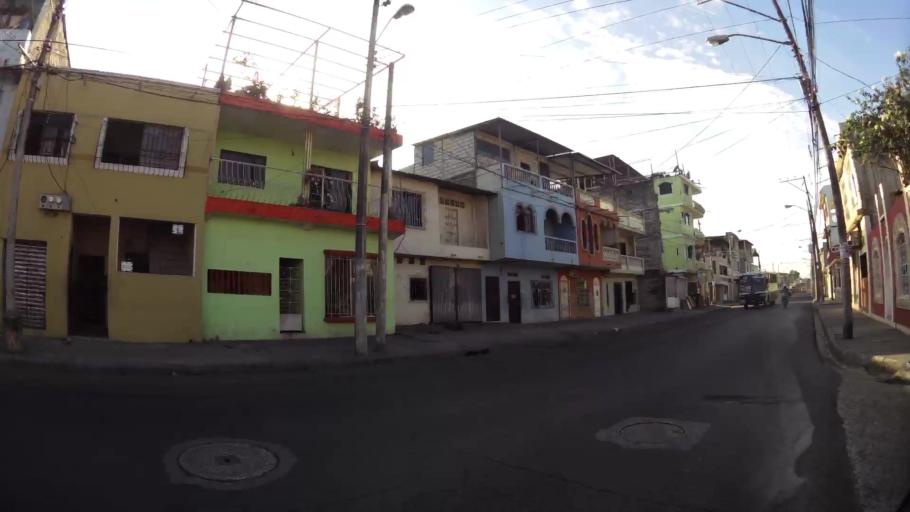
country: EC
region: Guayas
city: Guayaquil
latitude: -2.2285
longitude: -79.9061
